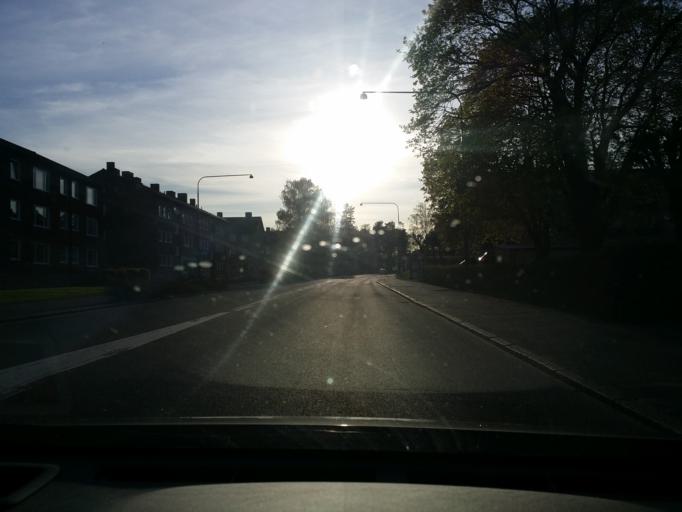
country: SE
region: Dalarna
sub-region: Avesta Kommun
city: Avesta
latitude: 60.1423
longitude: 16.1860
